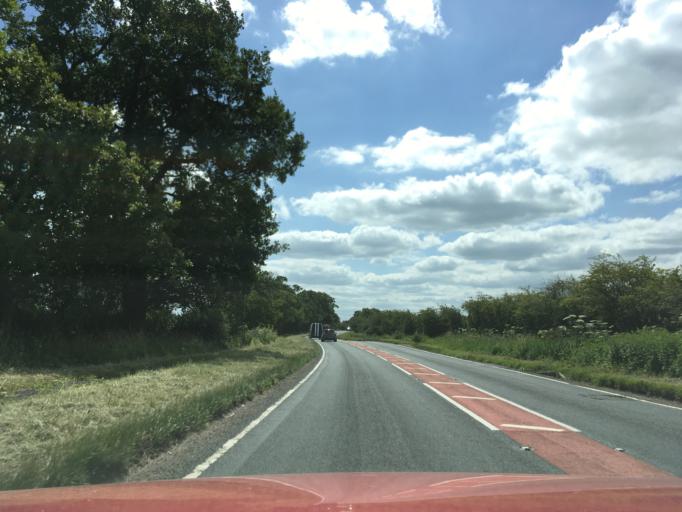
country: GB
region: England
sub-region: Buckinghamshire
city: Aylesbury
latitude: 51.8459
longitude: -0.8234
